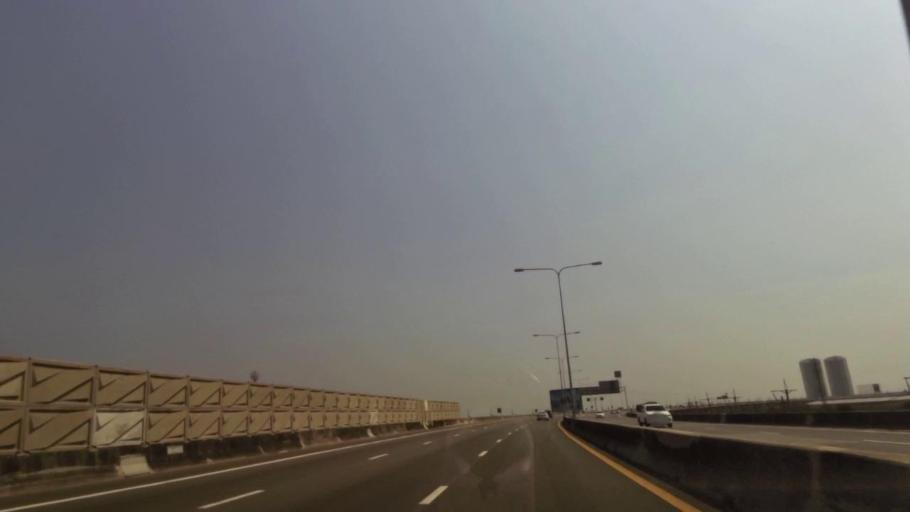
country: TH
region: Chachoengsao
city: Bang Pakong
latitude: 13.5018
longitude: 101.0021
